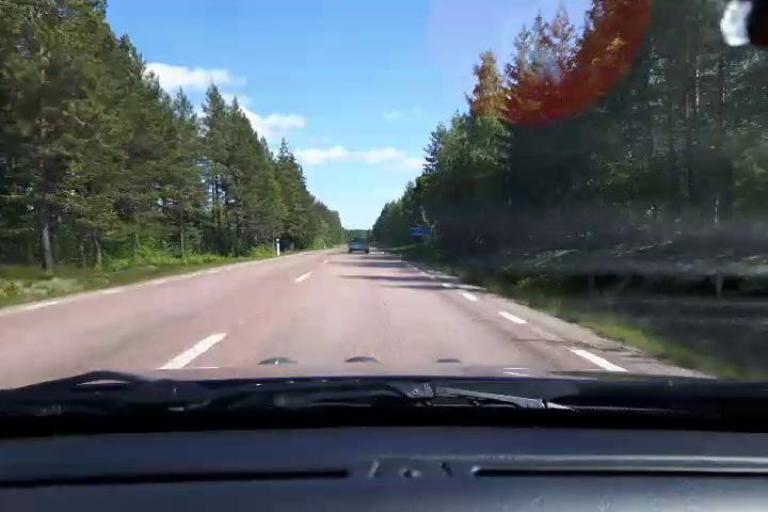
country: SE
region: Gaevleborg
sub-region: Hudiksvalls Kommun
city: Sorforsa
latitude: 61.7562
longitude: 16.8135
